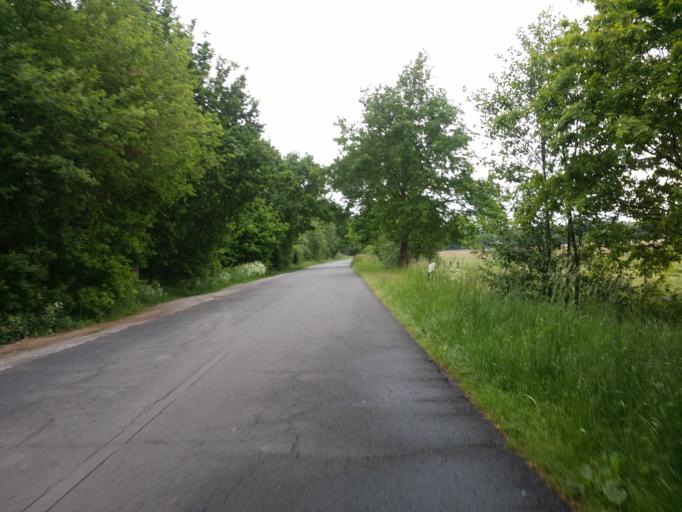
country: DE
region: Lower Saxony
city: Oldenburg
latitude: 53.1431
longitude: 8.2835
